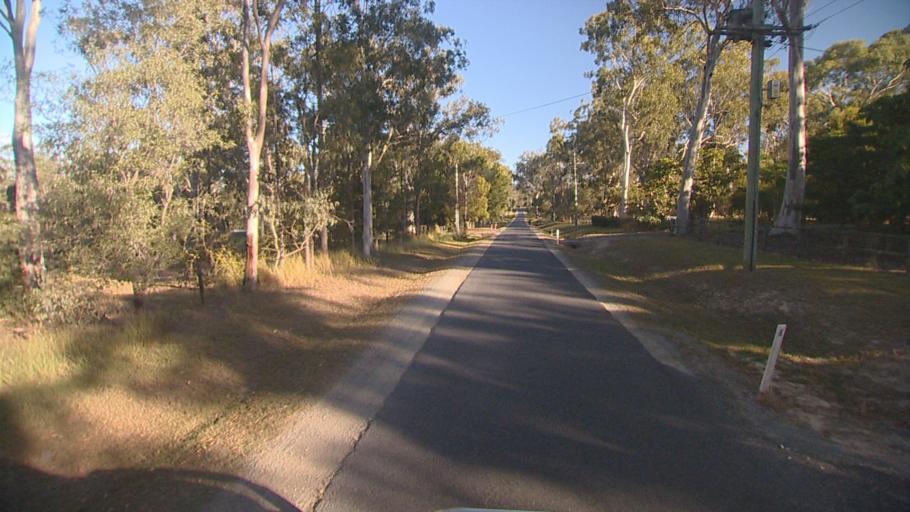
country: AU
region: Queensland
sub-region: Logan
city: Chambers Flat
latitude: -27.7874
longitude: 153.0860
